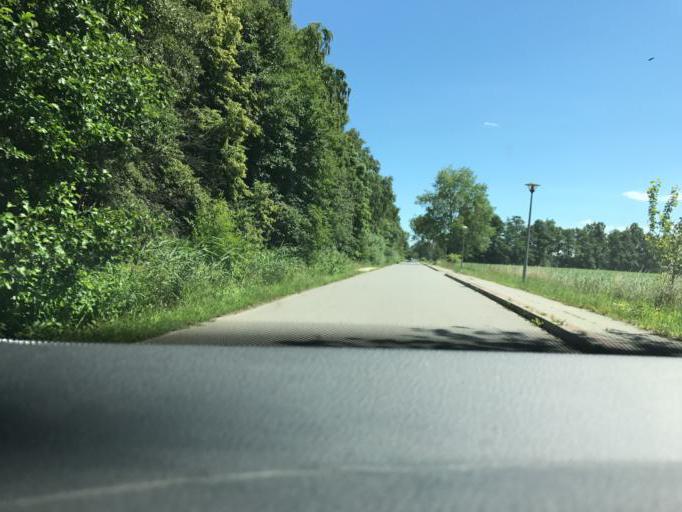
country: PL
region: Pomeranian Voivodeship
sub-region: Gdansk
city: Gdansk
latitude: 54.3281
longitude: 18.7344
